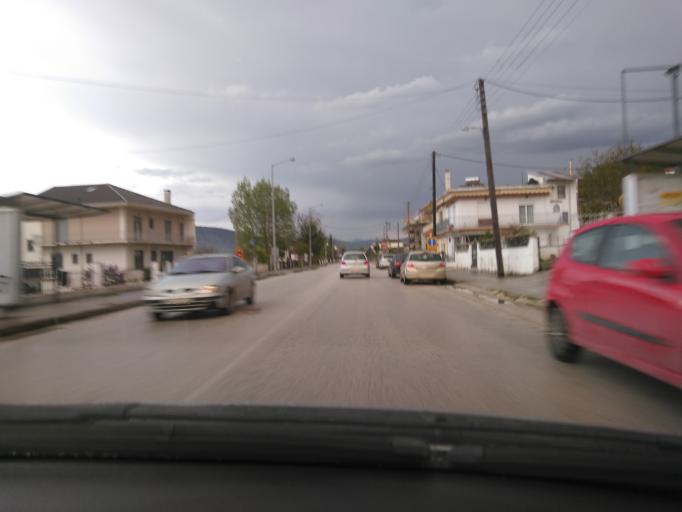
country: GR
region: Epirus
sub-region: Nomos Ioanninon
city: Katsikas
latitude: 39.6290
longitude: 20.8802
